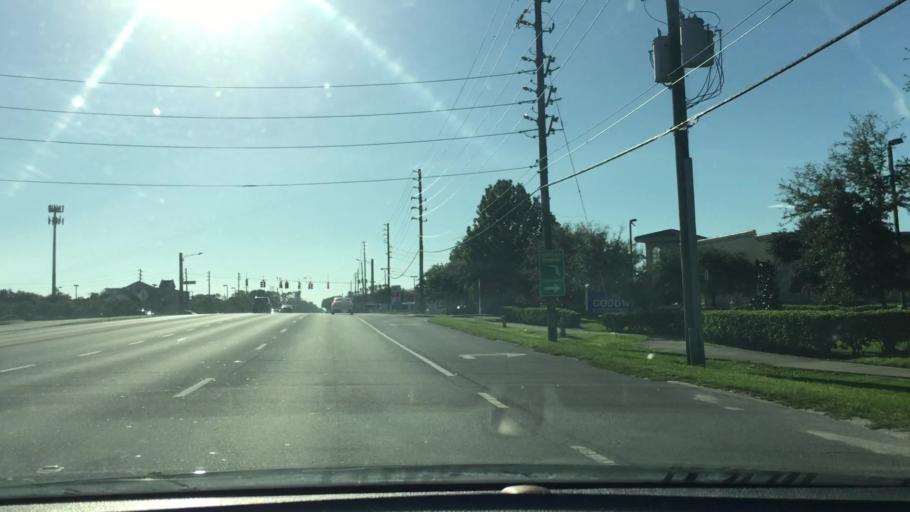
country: US
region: Florida
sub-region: Osceola County
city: Buenaventura Lakes
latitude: 28.3042
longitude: -81.3525
